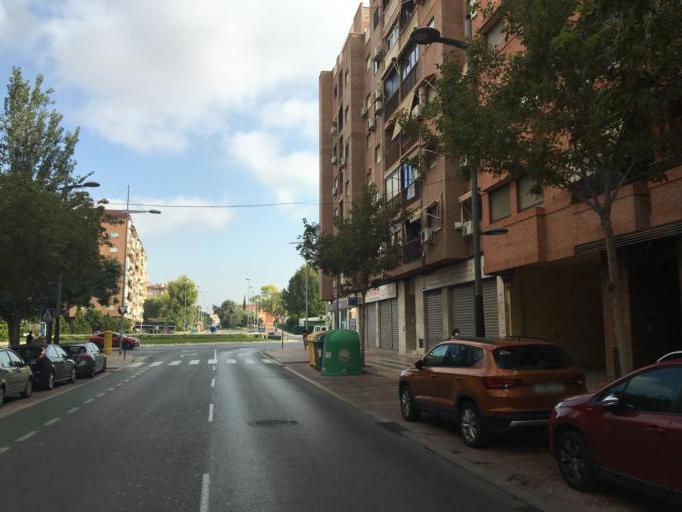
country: ES
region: Murcia
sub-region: Murcia
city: Cartagena
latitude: 37.6148
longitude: -0.9891
